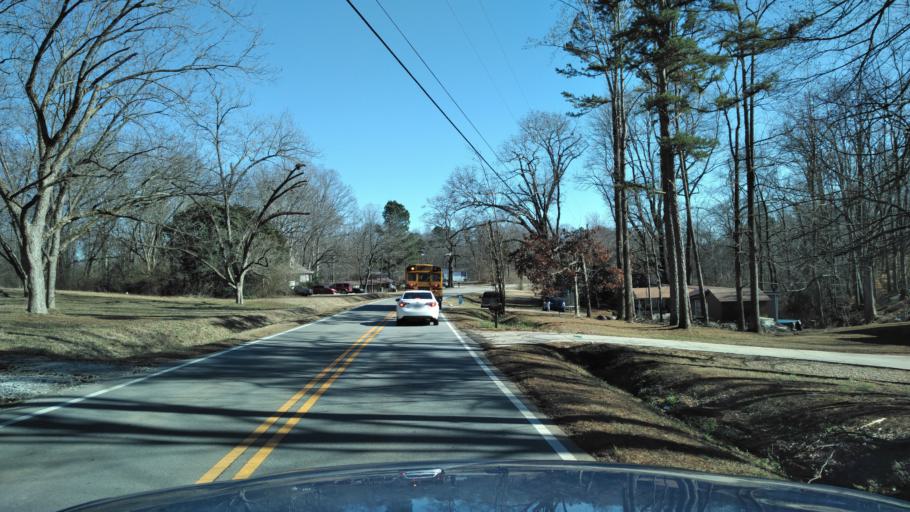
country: US
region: Georgia
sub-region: Hall County
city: Gainesville
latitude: 34.3173
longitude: -83.7564
